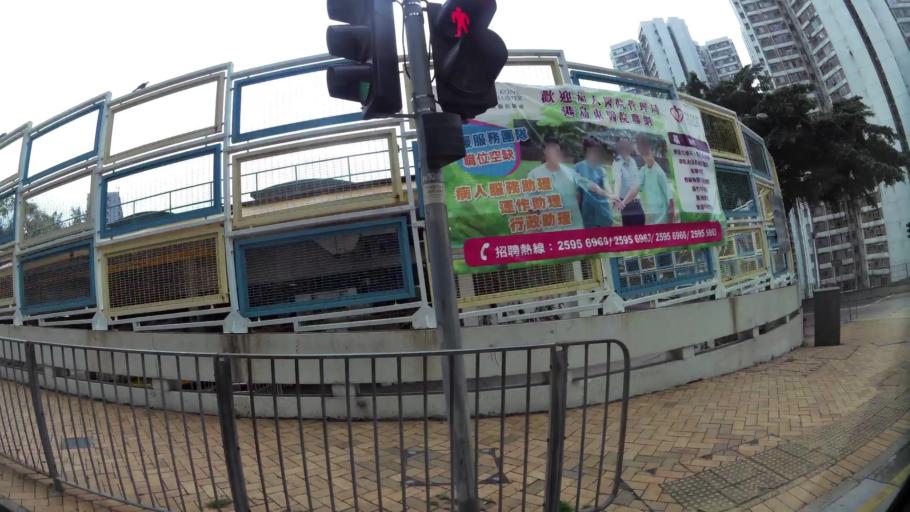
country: HK
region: Wanchai
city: Wan Chai
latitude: 22.2690
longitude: 114.2337
